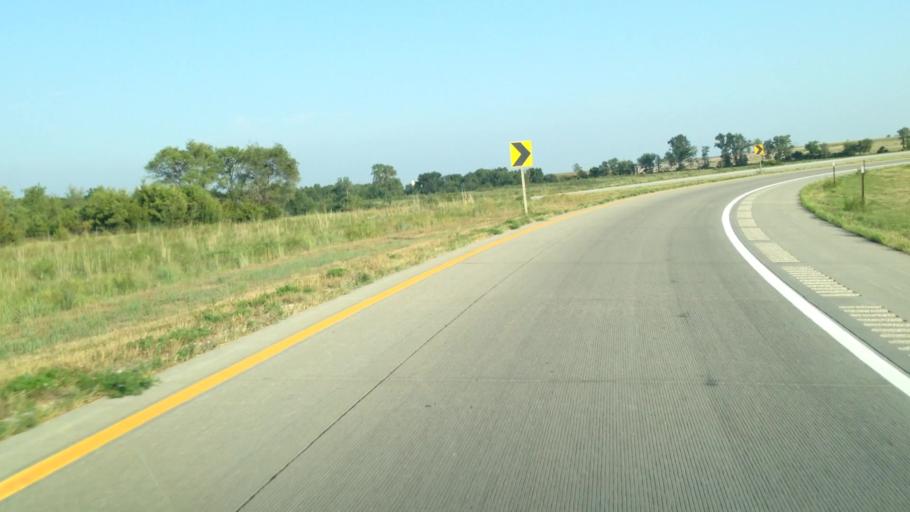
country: US
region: Kansas
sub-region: Franklin County
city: Ottawa
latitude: 38.6381
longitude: -95.2165
